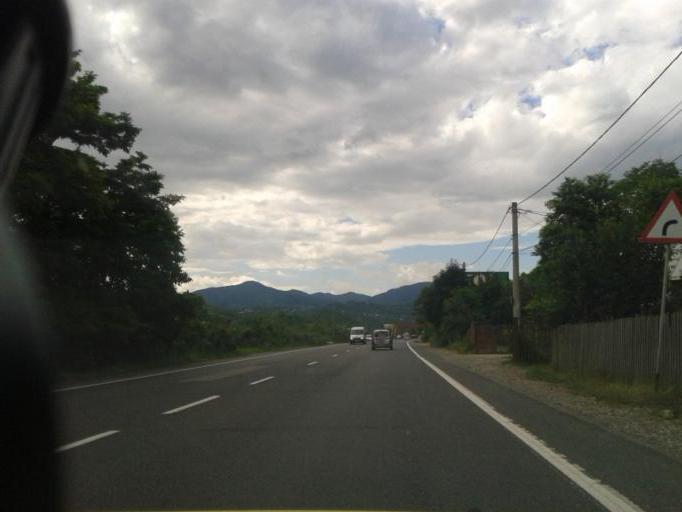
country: RO
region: Prahova
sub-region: Oras Breaza
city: Gura Beliei
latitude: 45.2116
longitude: 25.6550
